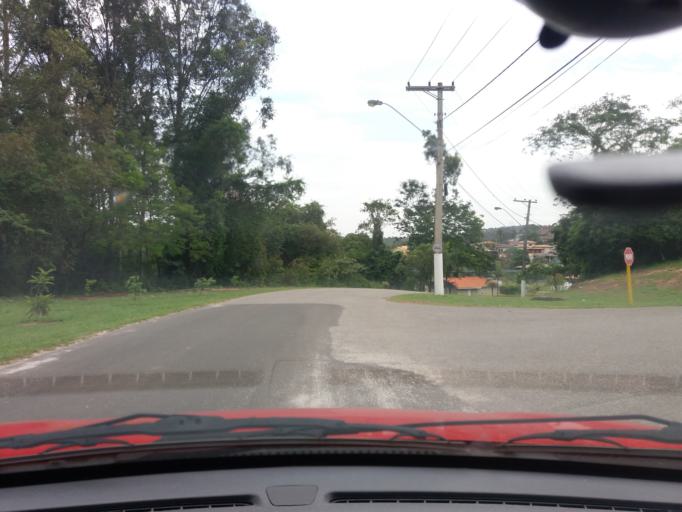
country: BR
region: Sao Paulo
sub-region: Itupeva
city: Itupeva
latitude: -23.2003
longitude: -47.0263
